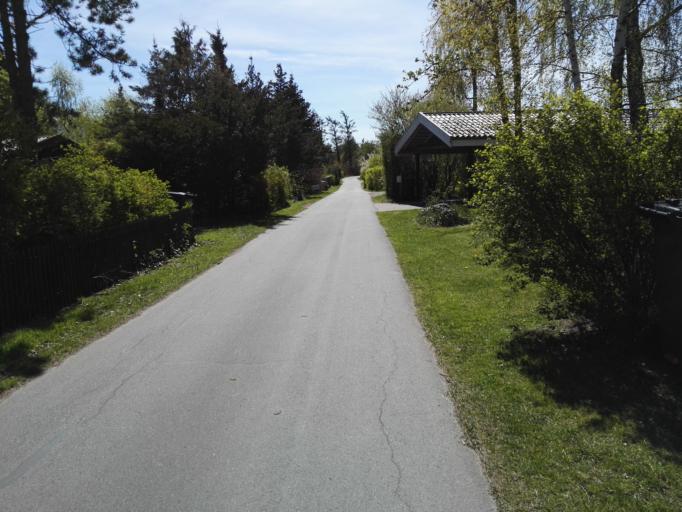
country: DK
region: Capital Region
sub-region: Frederikssund Kommune
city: Frederikssund
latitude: 55.8959
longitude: 12.0519
